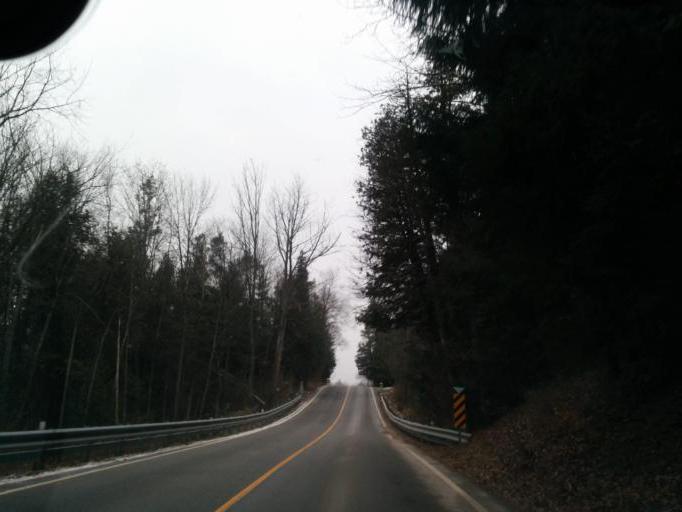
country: CA
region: Ontario
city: Orangeville
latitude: 43.8211
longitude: -79.9717
